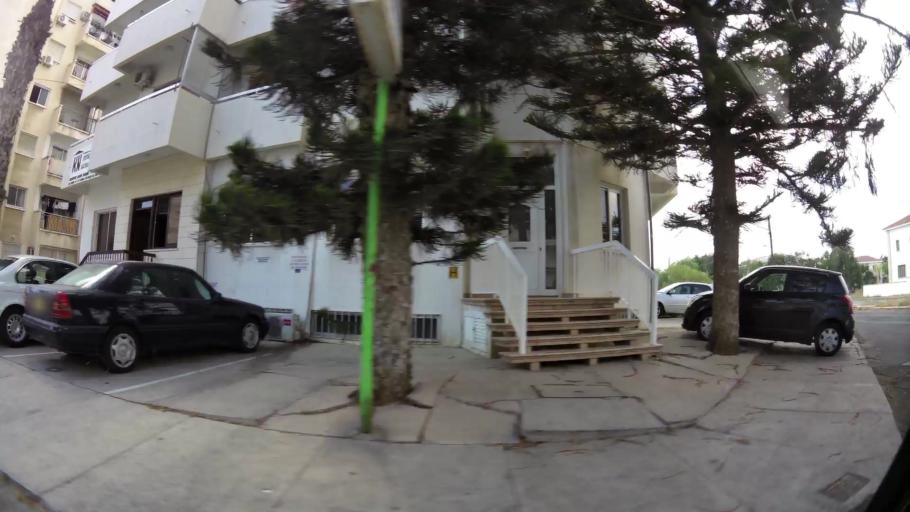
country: CY
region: Larnaka
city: Larnaca
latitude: 34.9132
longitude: 33.6266
